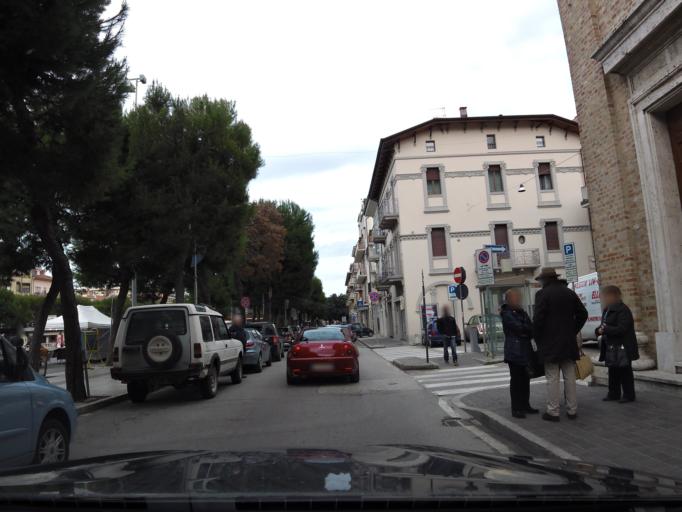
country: IT
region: The Marches
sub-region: Provincia di Macerata
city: Portocivitanova
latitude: 43.3068
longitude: 13.7293
